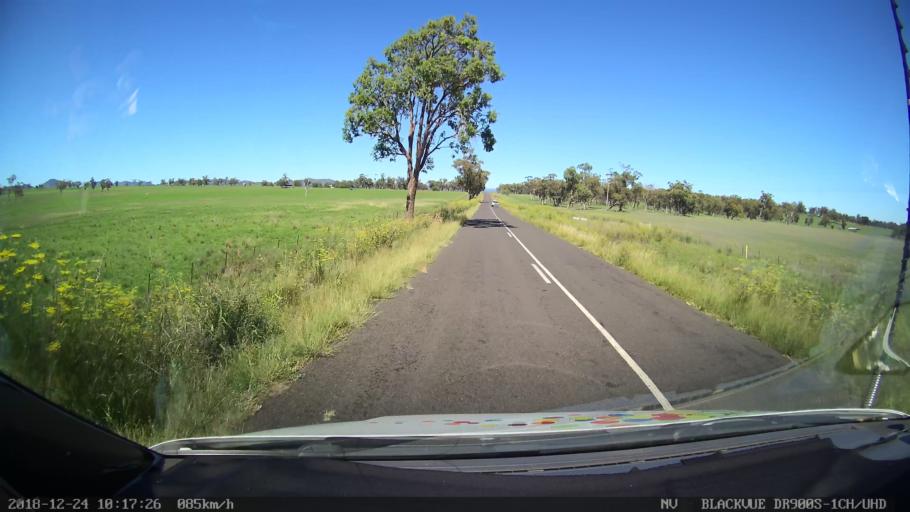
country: AU
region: New South Wales
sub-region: Liverpool Plains
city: Quirindi
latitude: -31.7200
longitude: 150.5913
